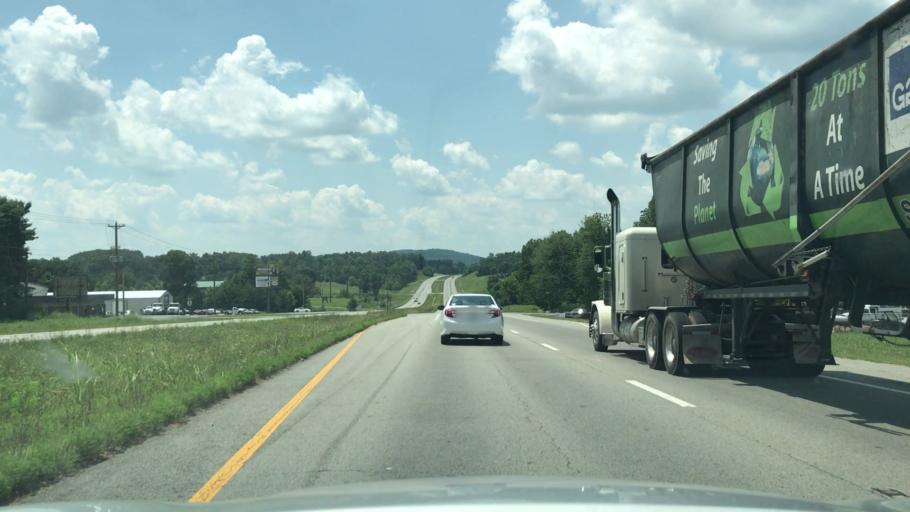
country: US
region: Tennessee
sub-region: Overton County
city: Livingston
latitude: 36.3534
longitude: -85.3440
